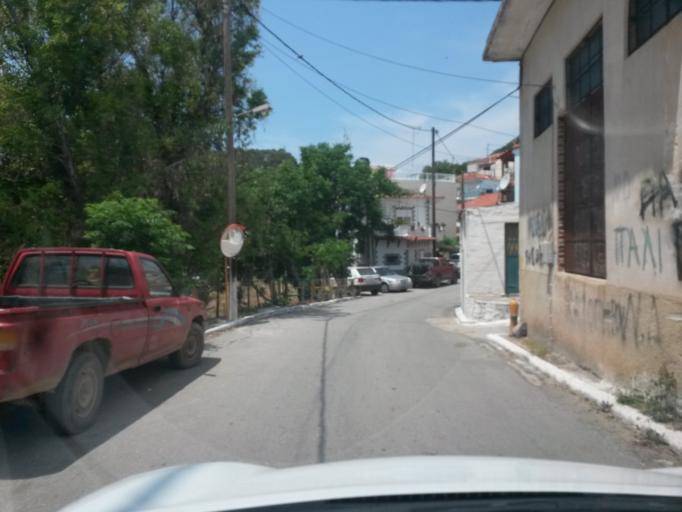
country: GR
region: North Aegean
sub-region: Nomos Lesvou
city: Pamfylla
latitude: 39.1813
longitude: 26.4183
